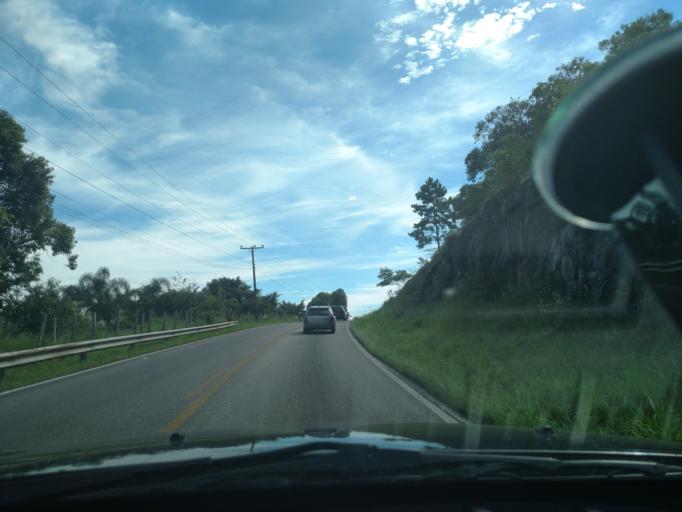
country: BR
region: Santa Catarina
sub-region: Tijucas
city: Tijucas
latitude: -27.3183
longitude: -48.5831
